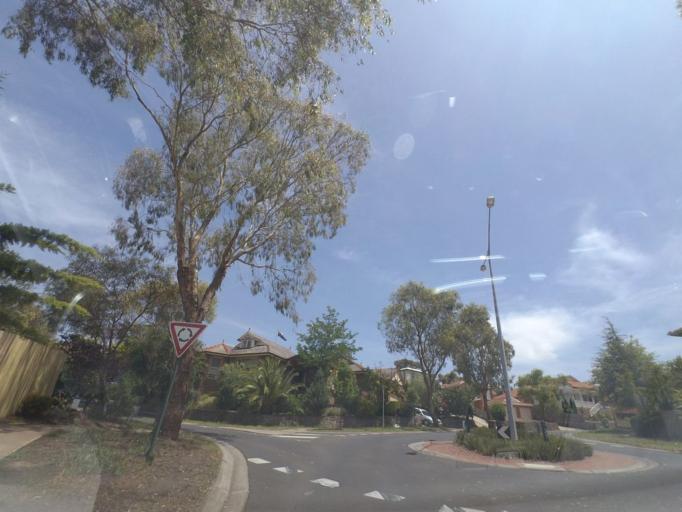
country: AU
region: Victoria
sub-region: Hume
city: Roxburgh Park
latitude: -37.6369
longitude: 144.9190
